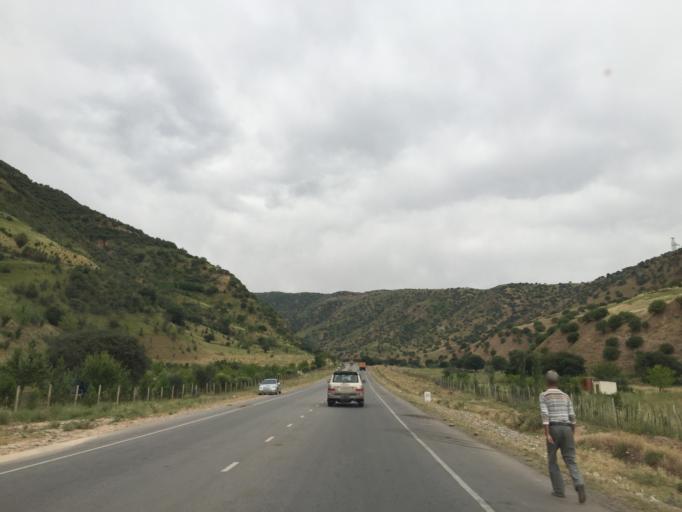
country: TJ
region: Khatlon
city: Norak
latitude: 38.3729
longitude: 69.2507
